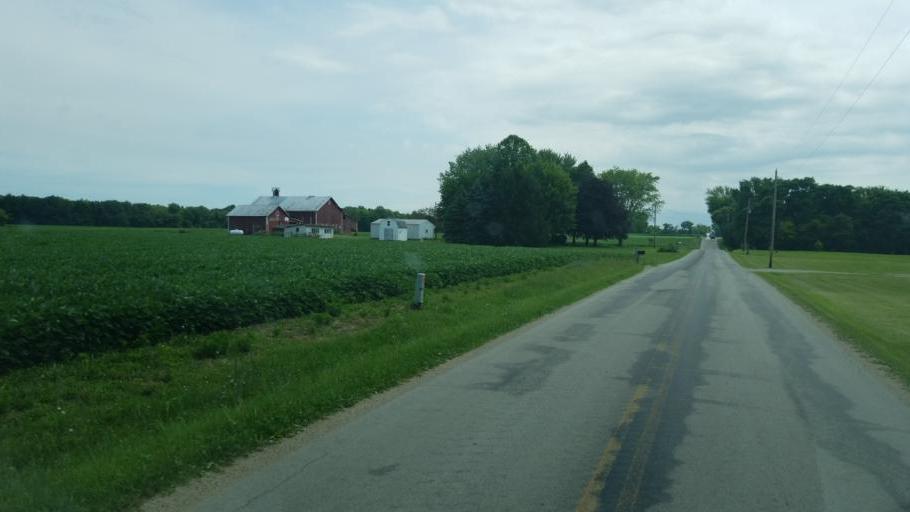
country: US
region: Ohio
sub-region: Wyandot County
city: Upper Sandusky
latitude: 40.8766
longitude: -83.2175
